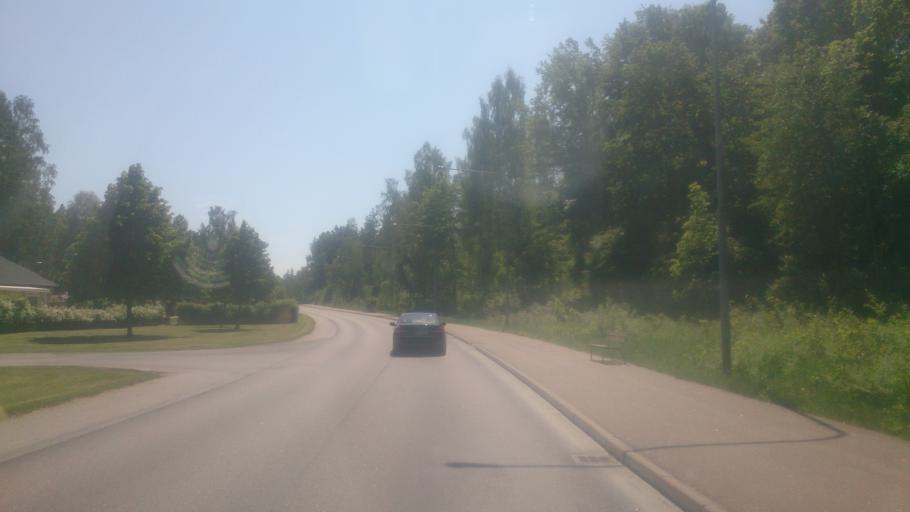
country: SE
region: OEstergoetland
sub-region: Atvidabergs Kommun
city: Atvidaberg
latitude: 58.1868
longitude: 16.0102
